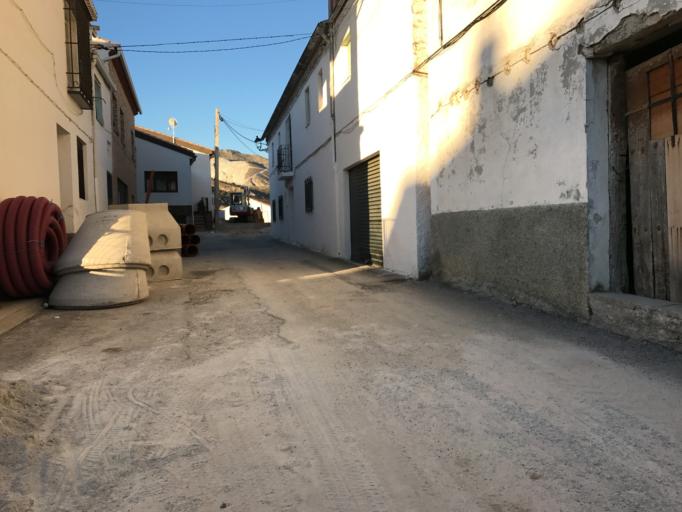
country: ES
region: Andalusia
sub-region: Provincia de Granada
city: Beas de Granada
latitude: 37.2187
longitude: -3.4805
